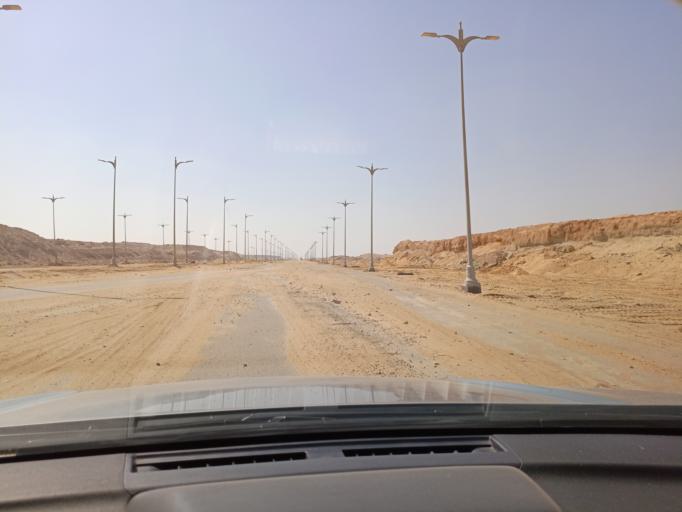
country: EG
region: Muhafazat al Qalyubiyah
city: Al Khankah
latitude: 30.0082
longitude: 31.6253
